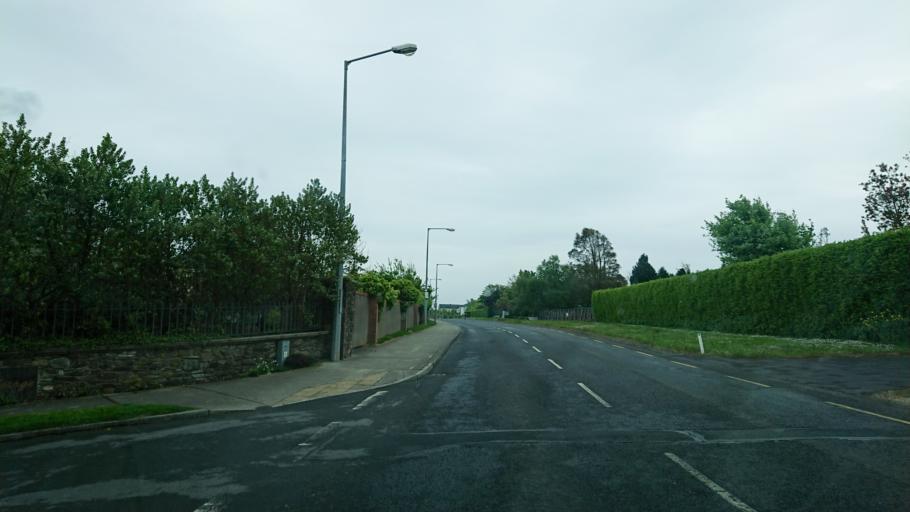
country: IE
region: Munster
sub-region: Waterford
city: Waterford
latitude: 52.2310
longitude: -7.0676
